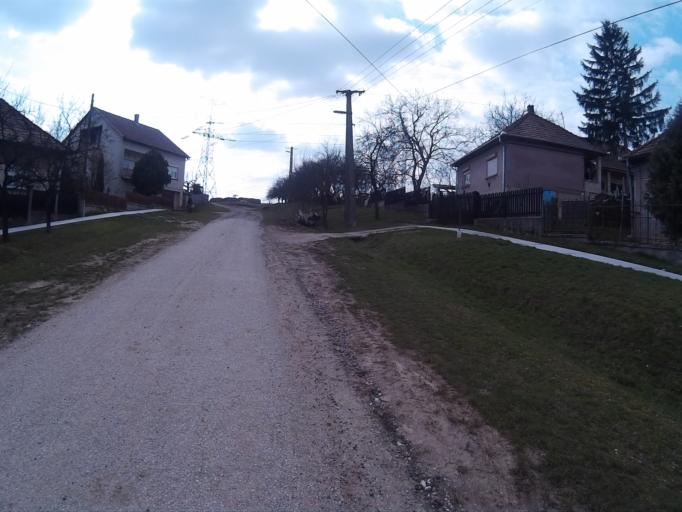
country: HU
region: Pest
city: Kosd
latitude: 47.8569
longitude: 19.1892
